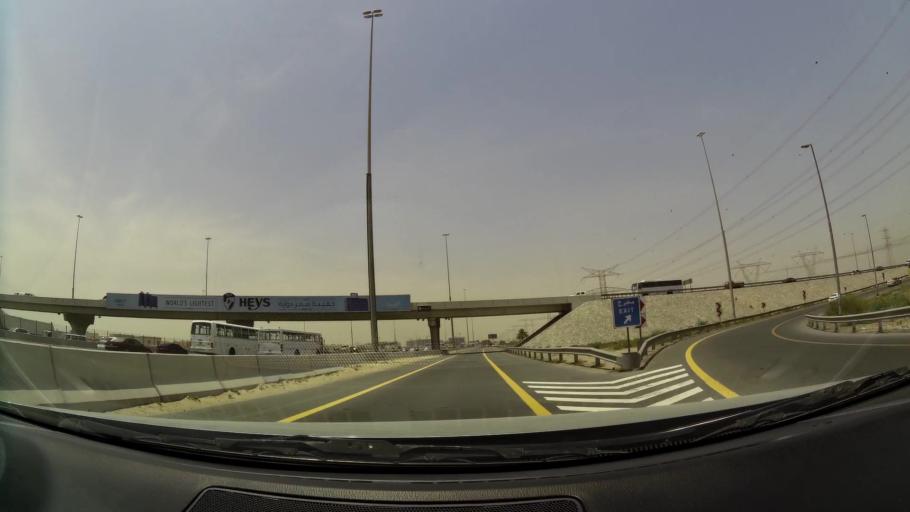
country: AE
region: Ash Shariqah
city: Sharjah
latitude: 25.2108
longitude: 55.4016
